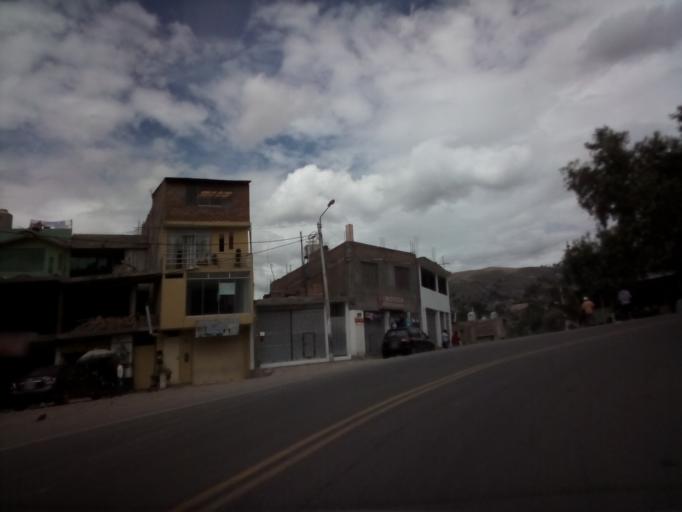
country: PE
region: Ayacucho
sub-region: Provincia de Huamanga
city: Ayacucho
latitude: -13.1563
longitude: -74.2339
